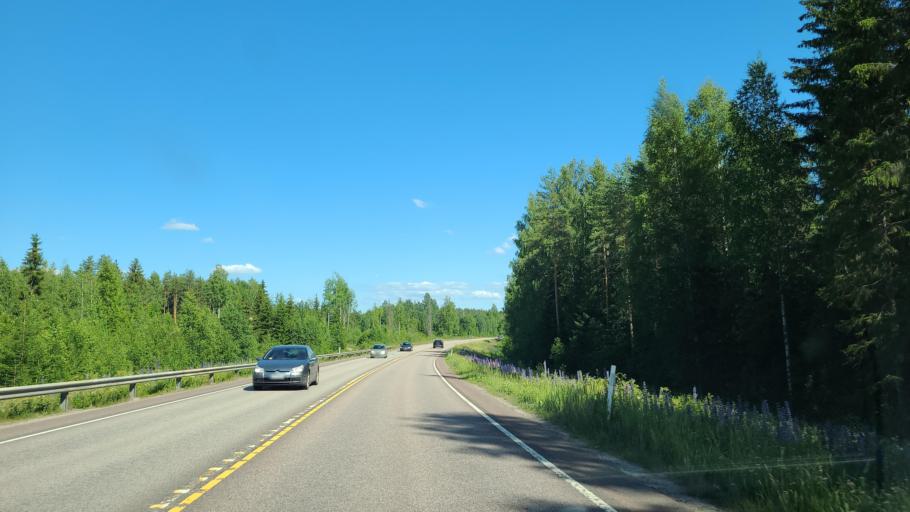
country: FI
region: Central Finland
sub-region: Jyvaeskylae
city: Petaejaevesi
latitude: 62.2736
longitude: 25.3589
